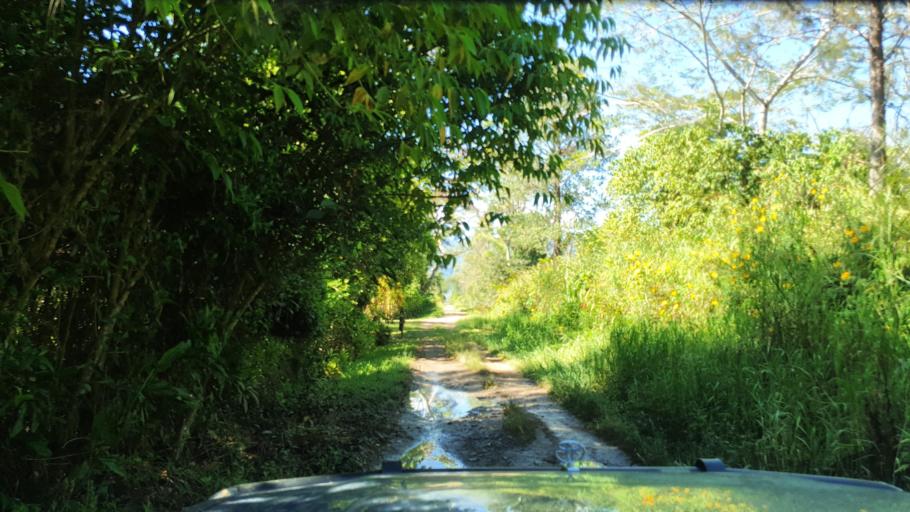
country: PG
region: Western Highlands
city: Rauna
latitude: -5.8061
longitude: 144.3755
